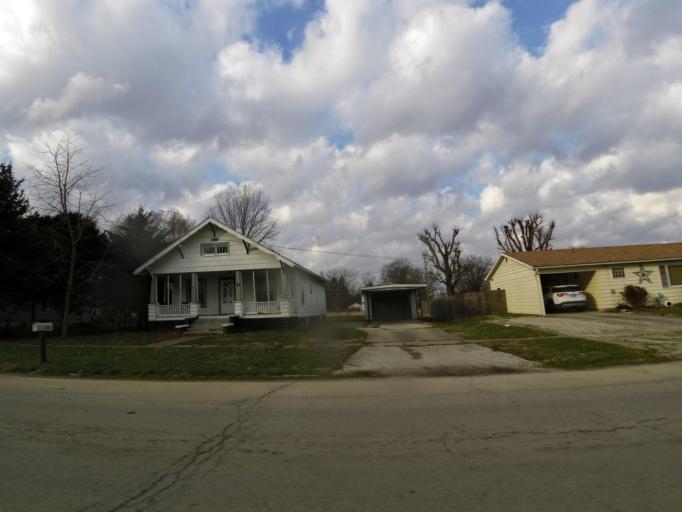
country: US
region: Illinois
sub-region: Fayette County
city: Ramsey
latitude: 39.1454
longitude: -89.1083
